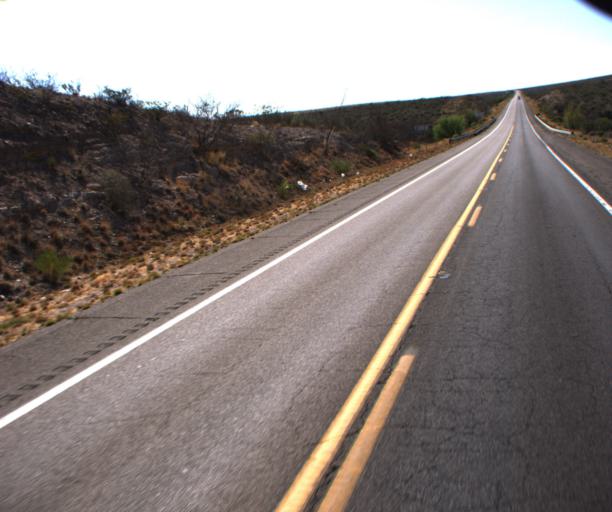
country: US
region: Arizona
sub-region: Cochise County
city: Tombstone
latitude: 31.7048
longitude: -110.0516
